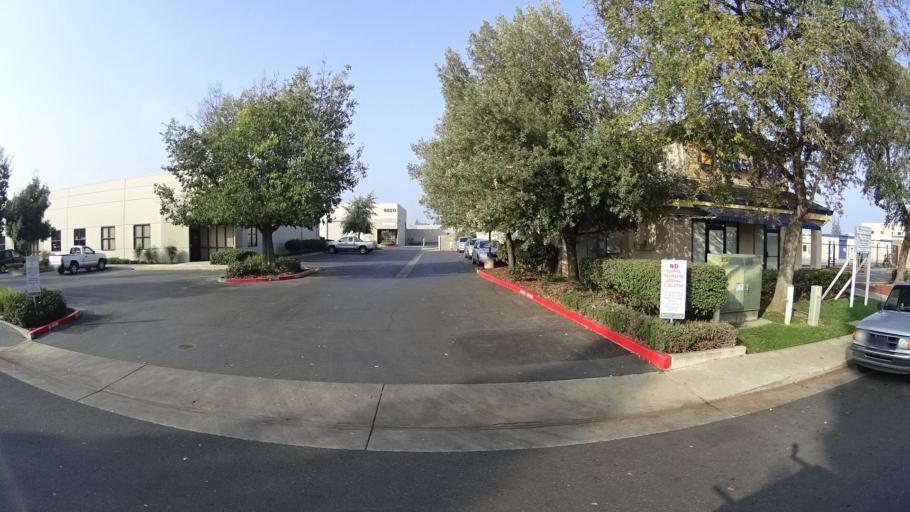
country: US
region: California
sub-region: Sacramento County
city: Elk Grove
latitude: 38.4012
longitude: -121.3569
